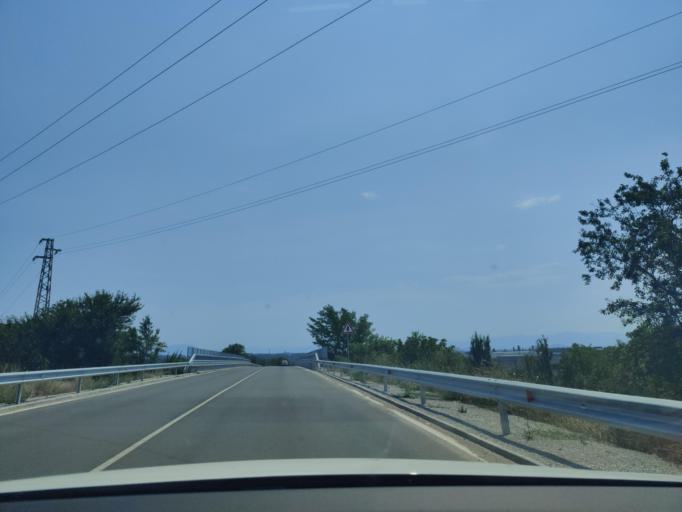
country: BG
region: Montana
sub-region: Obshtina Montana
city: Montana
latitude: 43.4295
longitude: 23.2379
